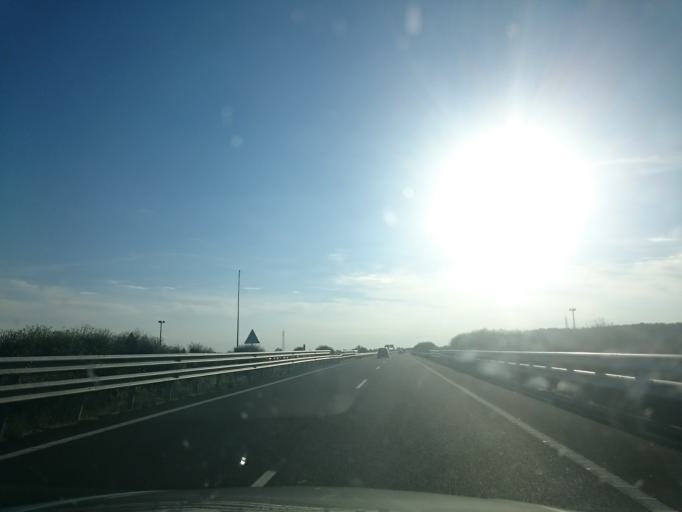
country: ES
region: Castille and Leon
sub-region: Provincia de Palencia
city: Carrion de los Condes
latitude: 42.3497
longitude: -4.6220
